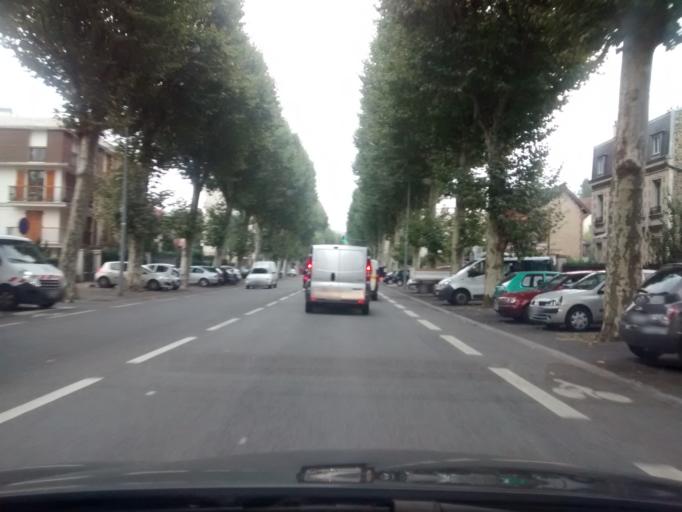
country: FR
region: Ile-de-France
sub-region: Departement des Yvelines
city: Viroflay
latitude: 48.8021
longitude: 2.1646
